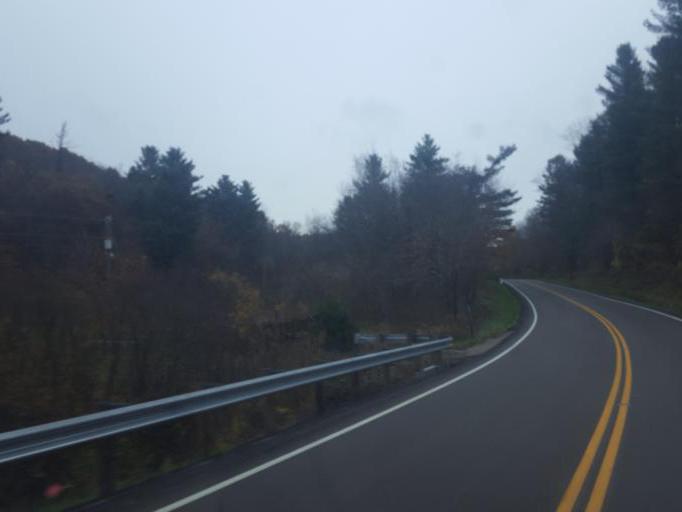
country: US
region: Ohio
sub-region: Knox County
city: Oak Hill
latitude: 40.4638
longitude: -82.1460
